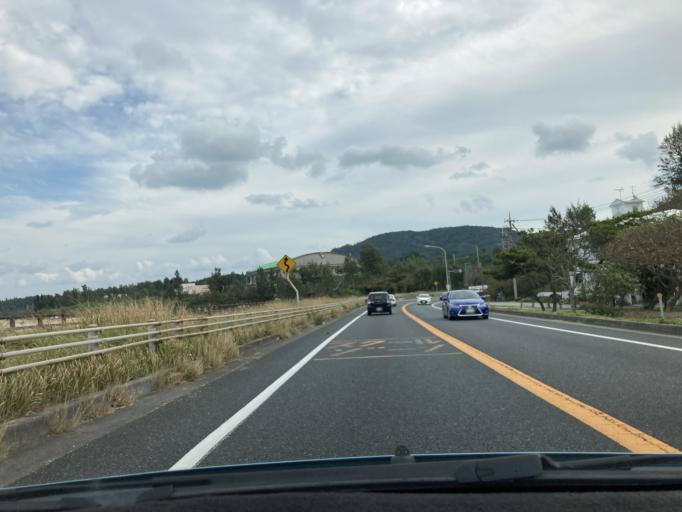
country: JP
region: Okinawa
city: Ishikawa
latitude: 26.5122
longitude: 127.8961
